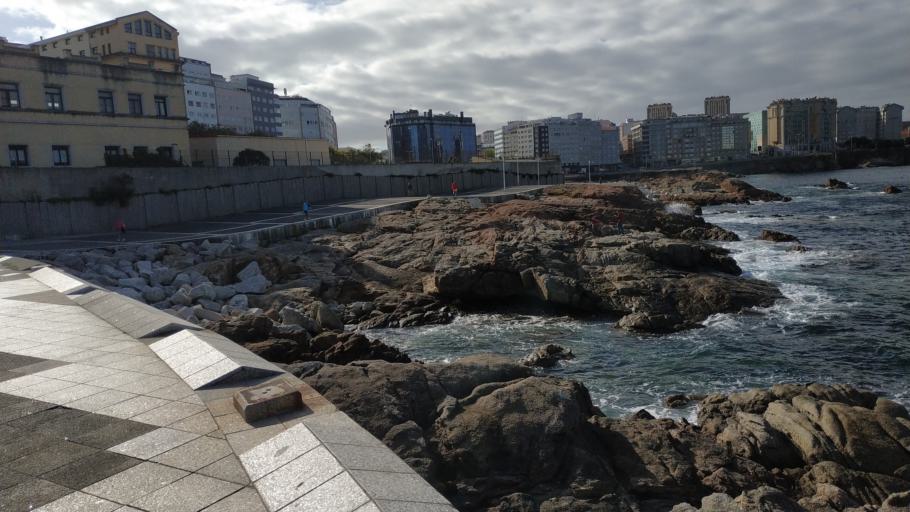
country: ES
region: Galicia
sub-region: Provincia da Coruna
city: A Coruna
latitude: 43.3708
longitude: -8.4145
